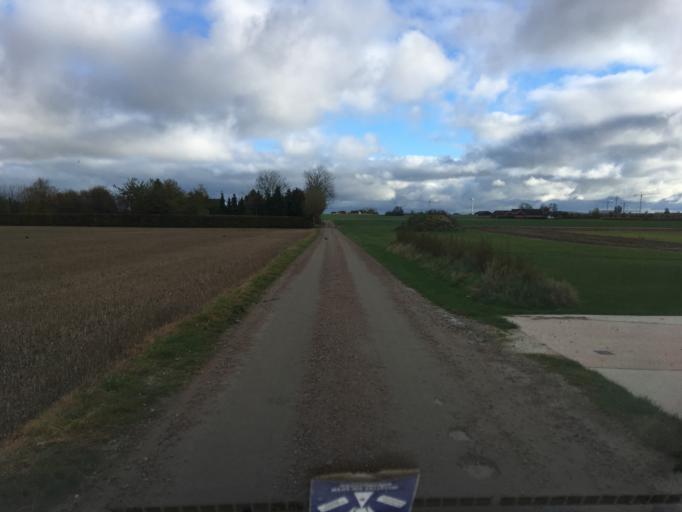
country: SE
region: Skane
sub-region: Lunds Kommun
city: Lund
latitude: 55.7401
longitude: 13.2151
